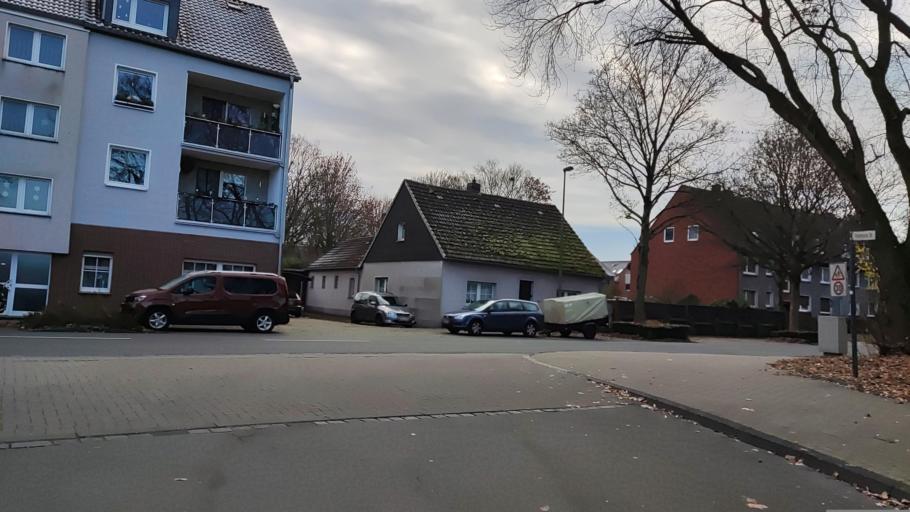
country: DE
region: North Rhine-Westphalia
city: Bochum-Hordel
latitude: 51.5363
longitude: 7.1887
